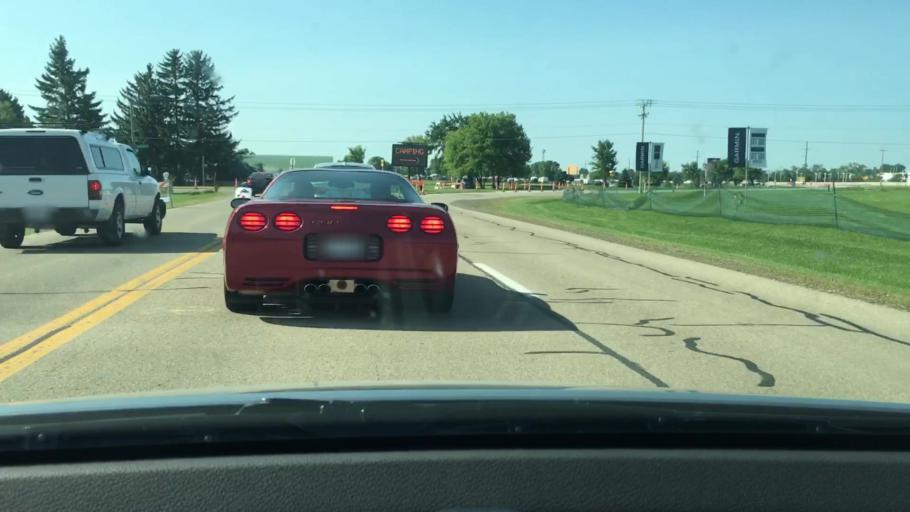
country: US
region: Wisconsin
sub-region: Winnebago County
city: Oshkosh
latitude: 43.9824
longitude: -88.5802
